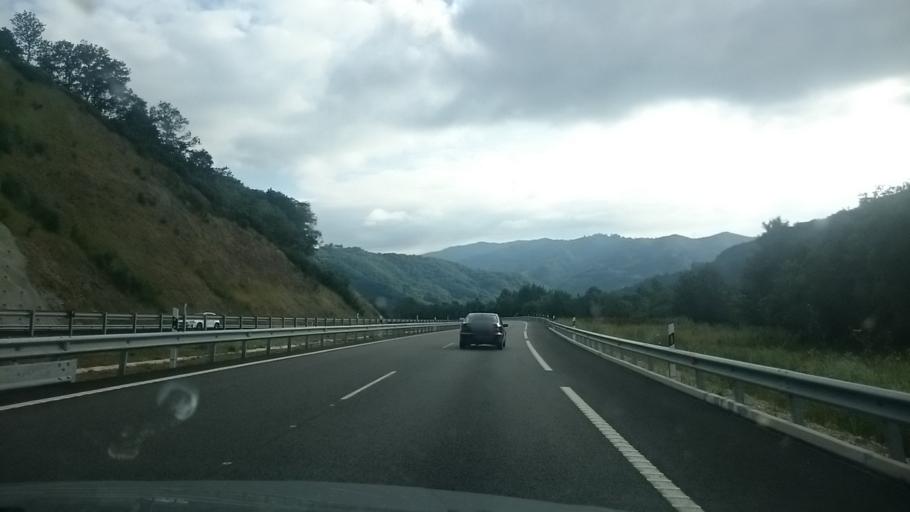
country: ES
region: Asturias
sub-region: Province of Asturias
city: Sama
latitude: 43.3347
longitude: -5.7107
